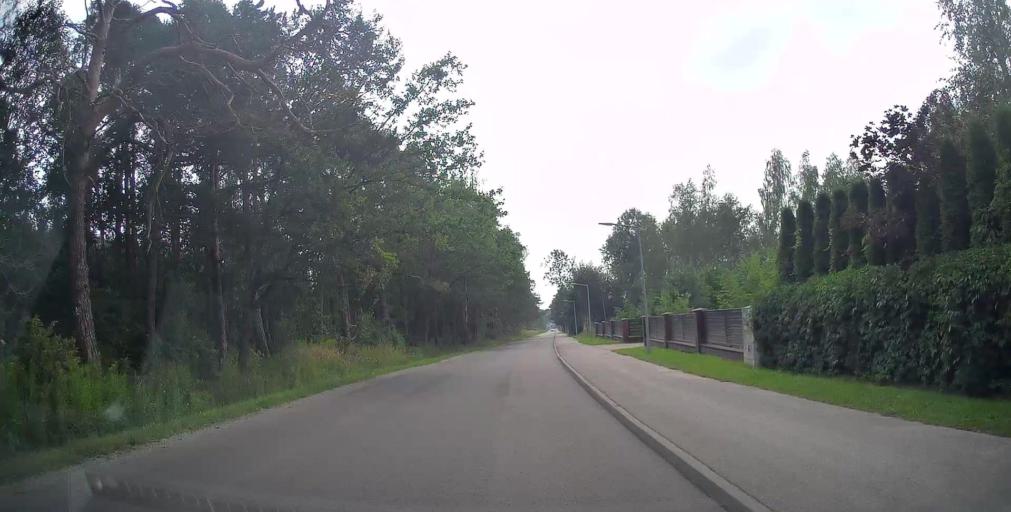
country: PL
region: Masovian Voivodeship
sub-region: Powiat bialobrzeski
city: Sucha
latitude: 51.6290
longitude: 20.9539
